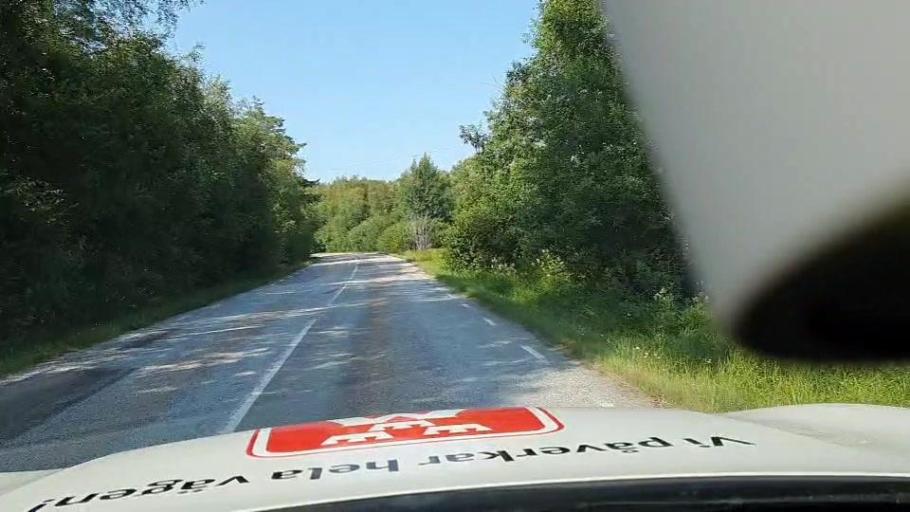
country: SE
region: Vaestra Goetaland
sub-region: Tjorns Kommun
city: Skaerhamn
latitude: 58.1039
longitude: 11.4858
